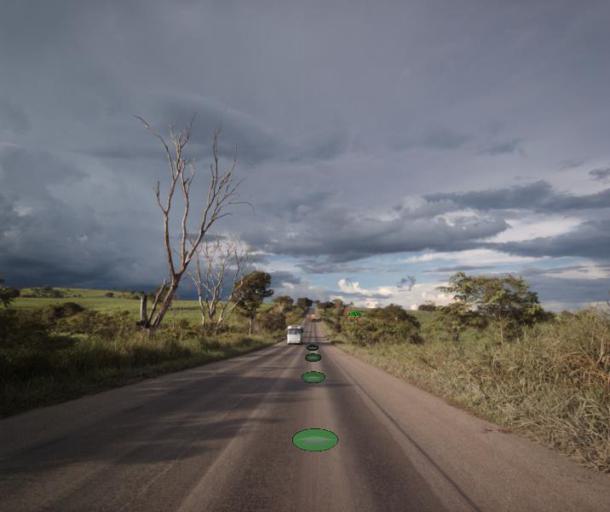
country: BR
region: Goias
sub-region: Itapaci
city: Itapaci
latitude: -15.1052
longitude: -49.4815
